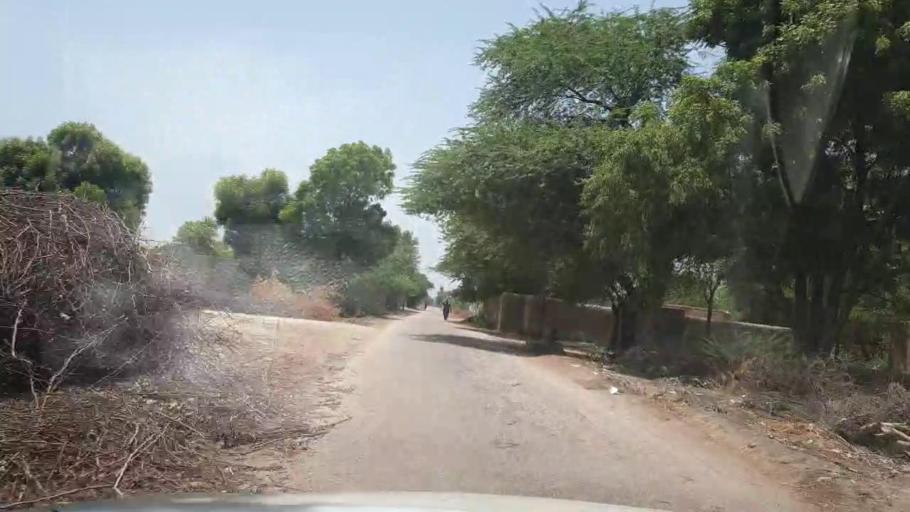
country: PK
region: Sindh
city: Bozdar
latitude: 27.1876
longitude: 68.6149
